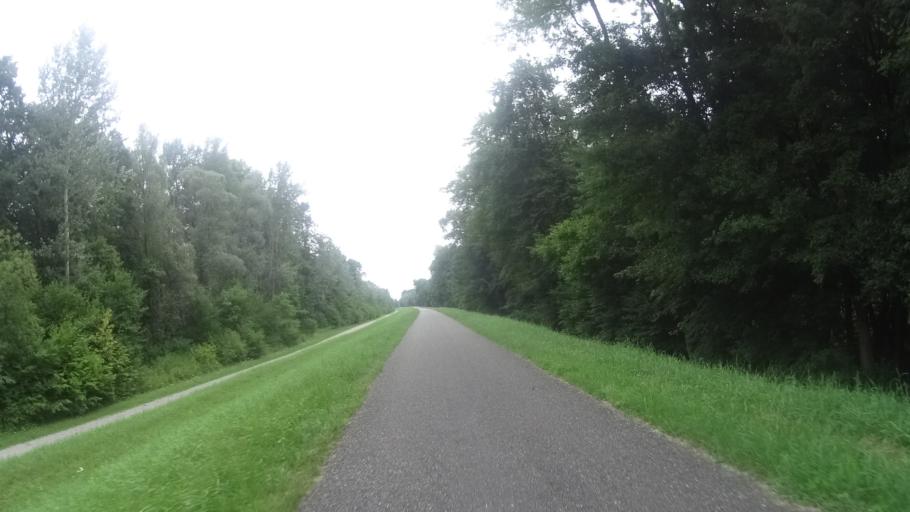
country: DE
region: Baden-Wuerttemberg
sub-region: Karlsruhe Region
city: Steinmauern
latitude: 48.9370
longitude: 8.1783
